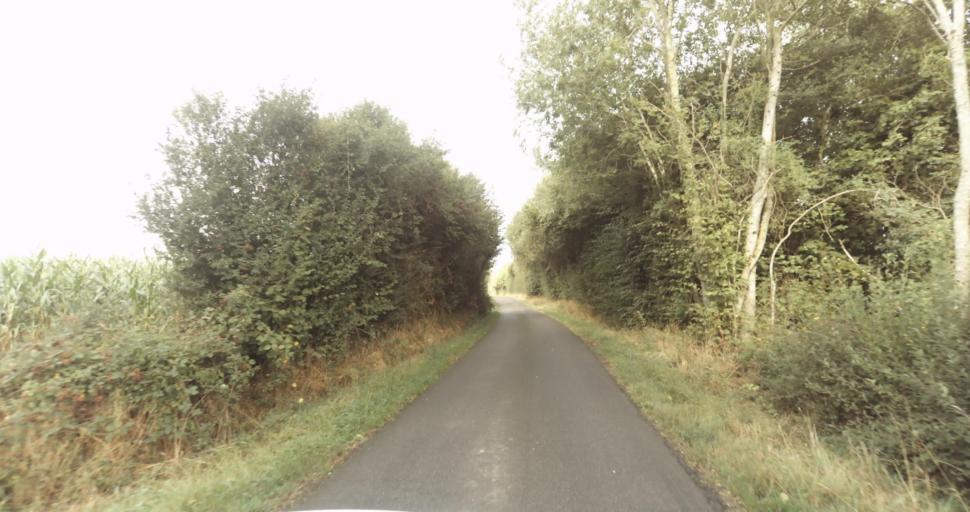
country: FR
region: Lower Normandy
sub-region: Departement de l'Orne
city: Gace
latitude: 48.8550
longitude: 0.3557
